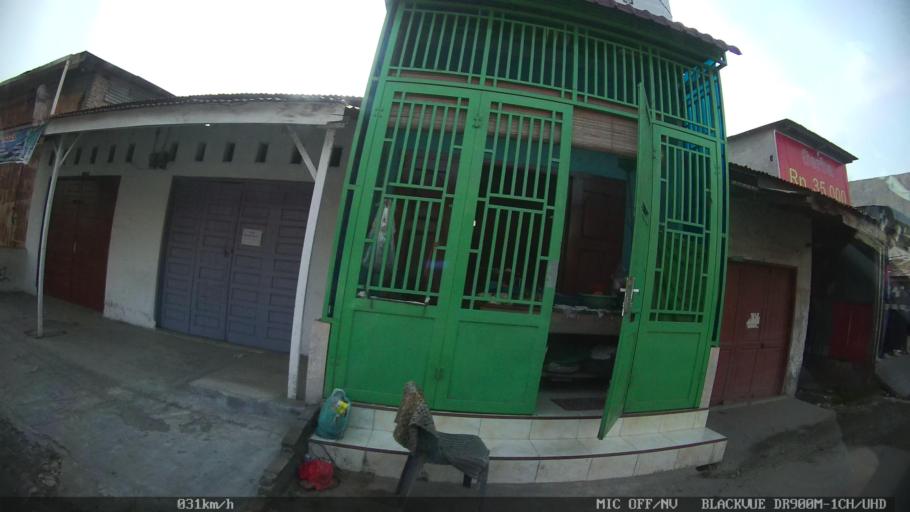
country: ID
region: North Sumatra
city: Medan
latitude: 3.5794
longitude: 98.7566
